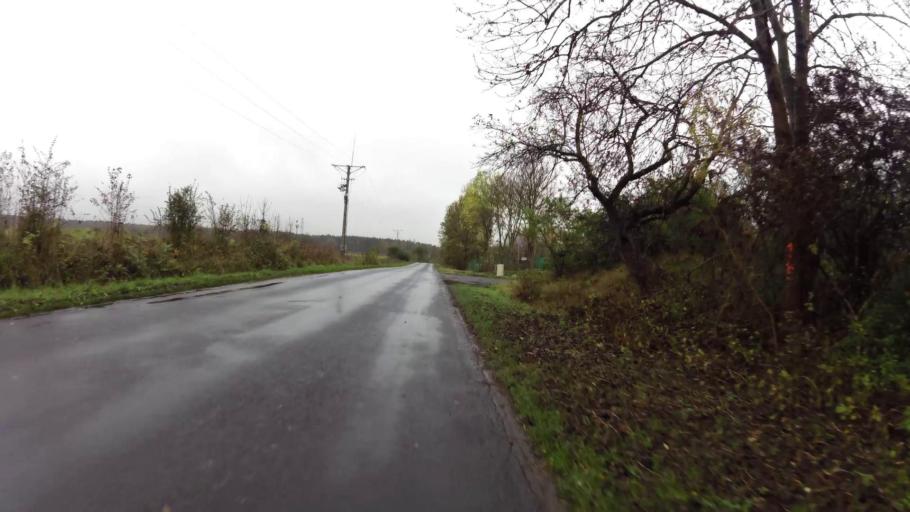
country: PL
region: West Pomeranian Voivodeship
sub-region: Powiat gryfinski
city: Gryfino
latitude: 53.2370
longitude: 14.5142
